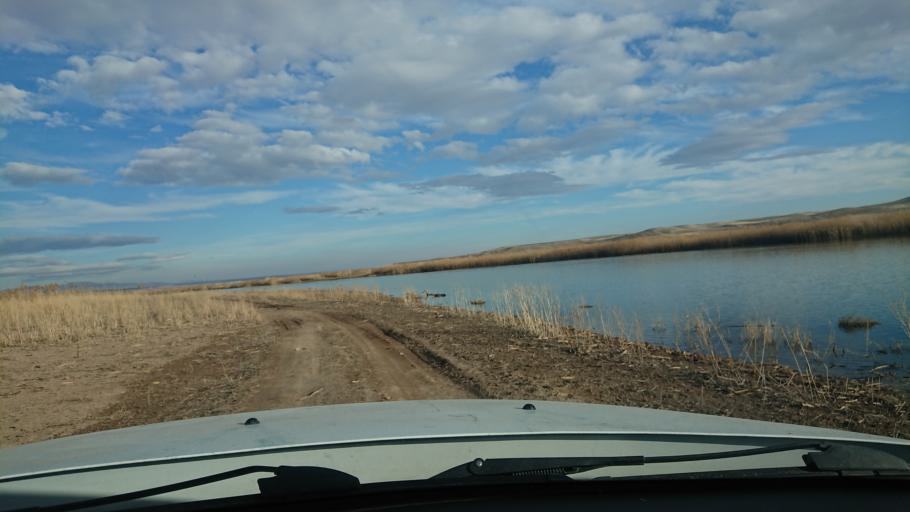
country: TR
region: Aksaray
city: Sariyahsi
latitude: 39.0343
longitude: 33.9628
